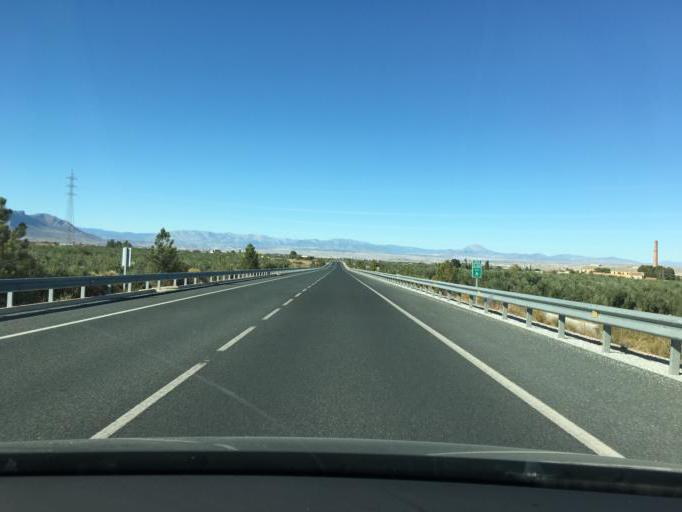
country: ES
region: Andalusia
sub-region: Provincia de Granada
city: Caniles
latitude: 37.4593
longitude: -2.7374
